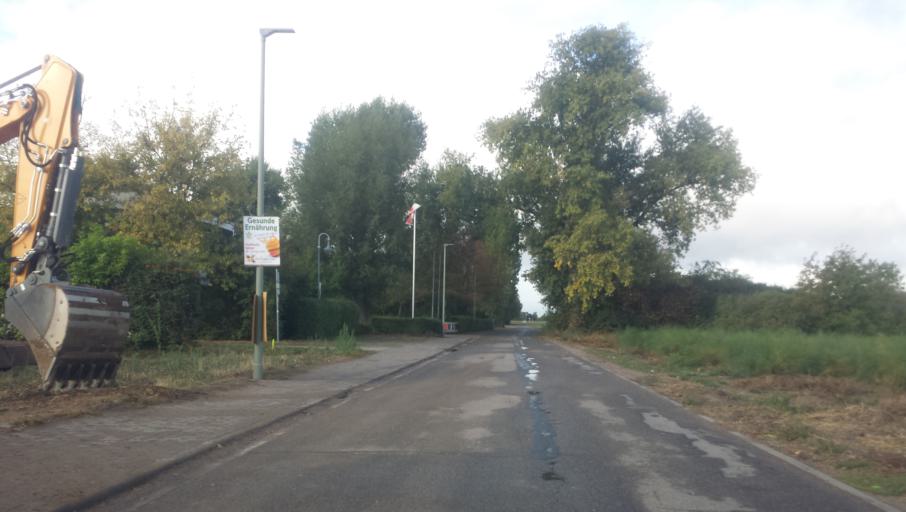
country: DE
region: Rheinland-Pfalz
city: Bohl-Iggelheim
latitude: 49.3744
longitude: 8.3059
